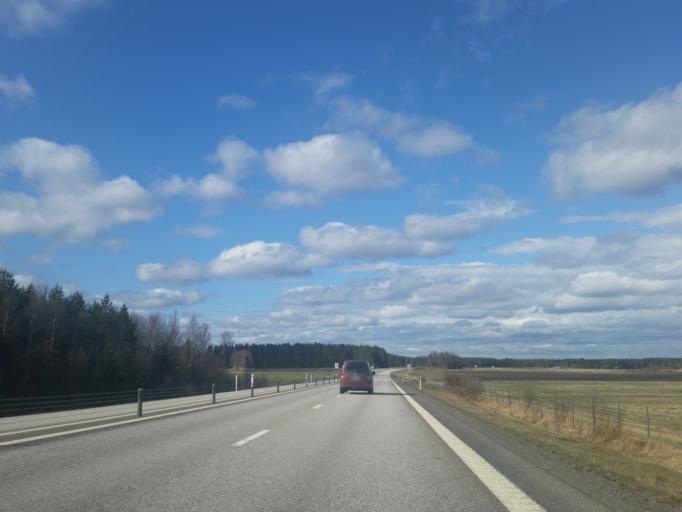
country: SE
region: Vaesterbotten
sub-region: Robertsfors Kommun
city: Robertsfors
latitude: 64.0952
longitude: 20.8693
